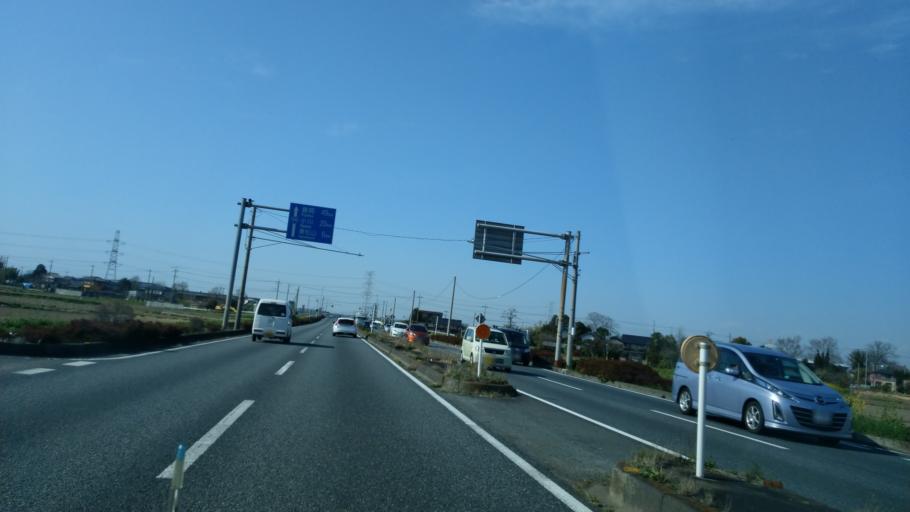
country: JP
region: Saitama
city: Sakado
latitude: 35.9972
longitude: 139.4533
